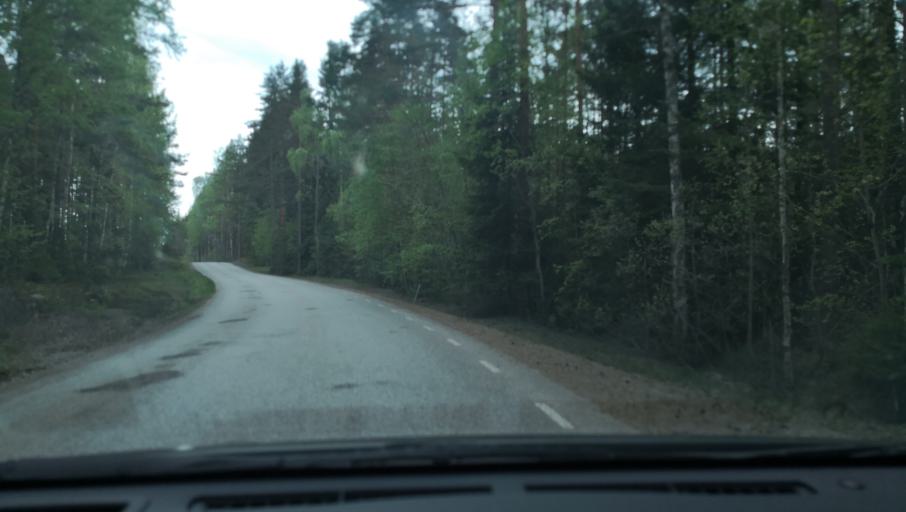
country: SE
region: Vaestmanland
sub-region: Skinnskattebergs Kommun
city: Skinnskatteberg
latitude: 59.8167
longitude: 15.5541
